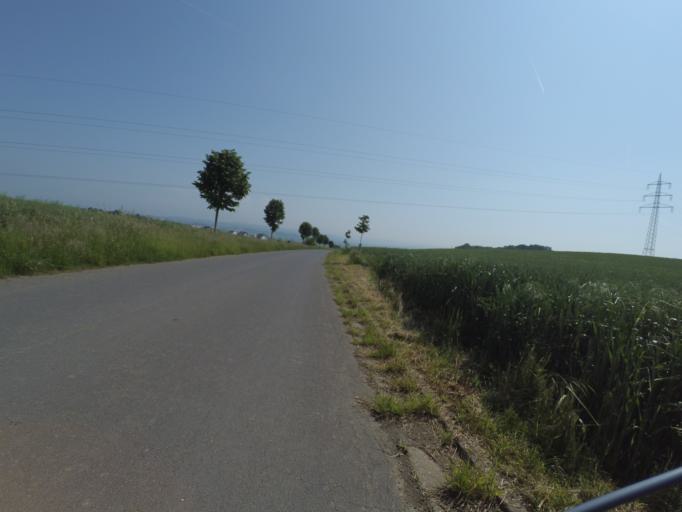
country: DE
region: Rheinland-Pfalz
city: Kollig
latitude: 50.2600
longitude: 7.2752
